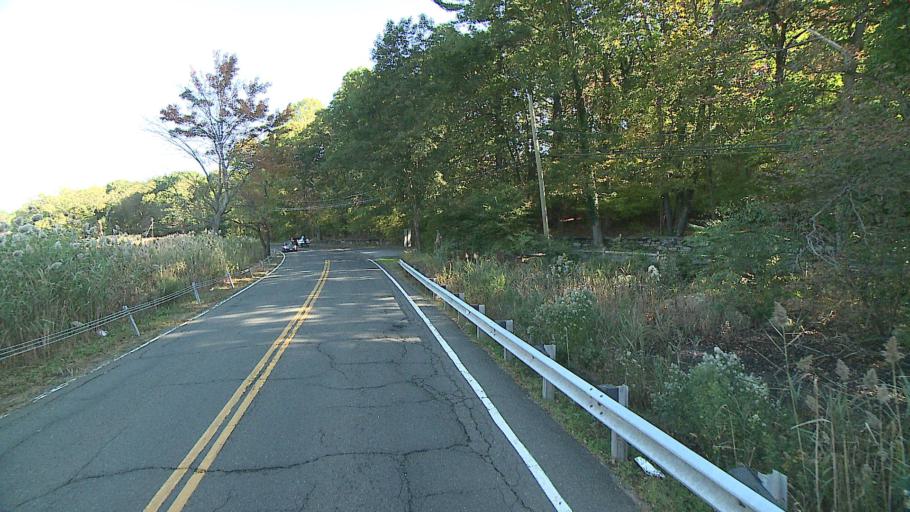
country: US
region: Connecticut
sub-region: Fairfield County
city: Darien
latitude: 41.0724
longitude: -73.4285
